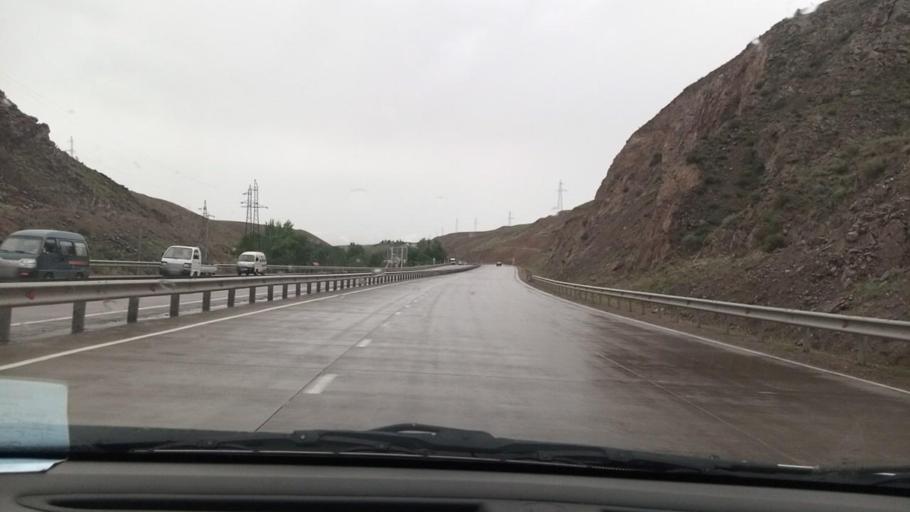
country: TJ
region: Viloyati Sughd
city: Shaydon
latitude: 40.9543
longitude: 70.6740
